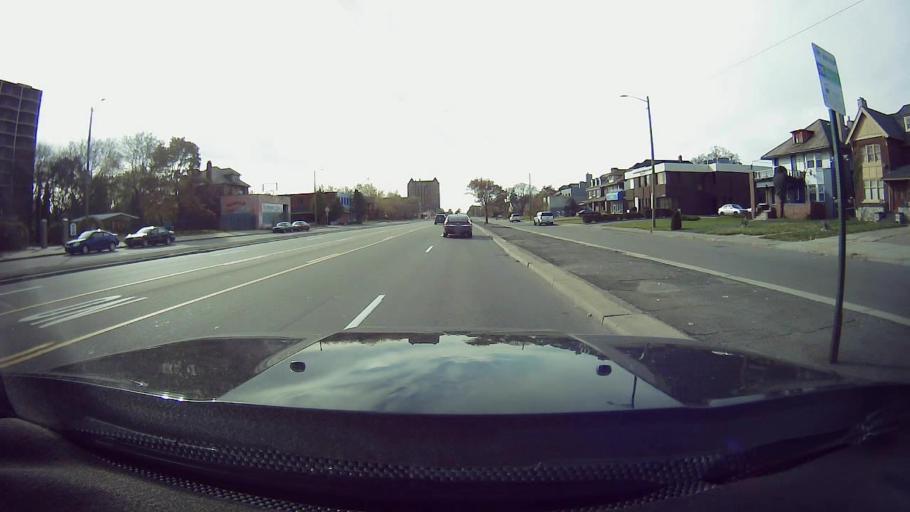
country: US
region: Michigan
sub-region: Wayne County
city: Highland Park
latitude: 42.3622
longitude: -83.0950
